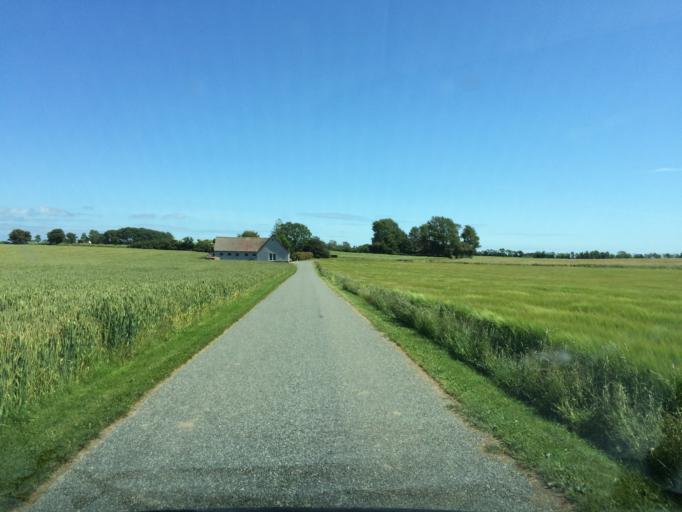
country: DK
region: Central Jutland
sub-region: Samso Kommune
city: Tranebjerg
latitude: 55.8361
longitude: 10.5331
